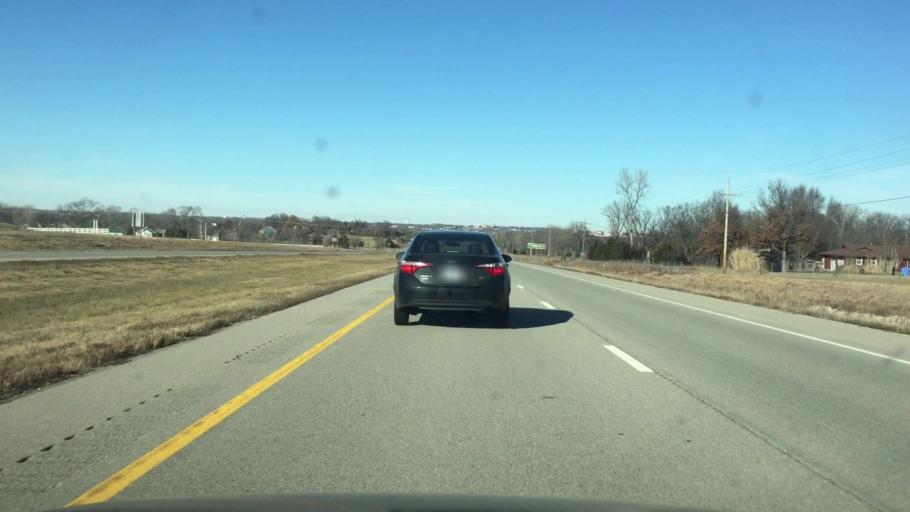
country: US
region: Kansas
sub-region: Douglas County
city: Lawrence
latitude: 38.8955
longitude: -95.2604
